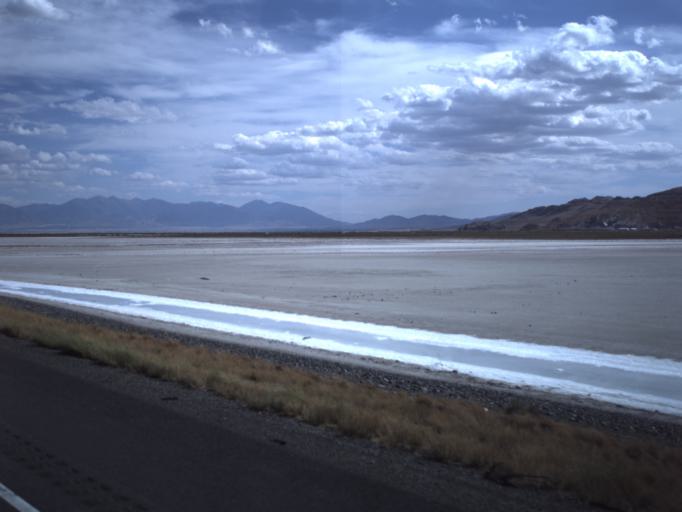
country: US
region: Utah
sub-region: Tooele County
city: Grantsville
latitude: 40.7284
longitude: -112.5841
